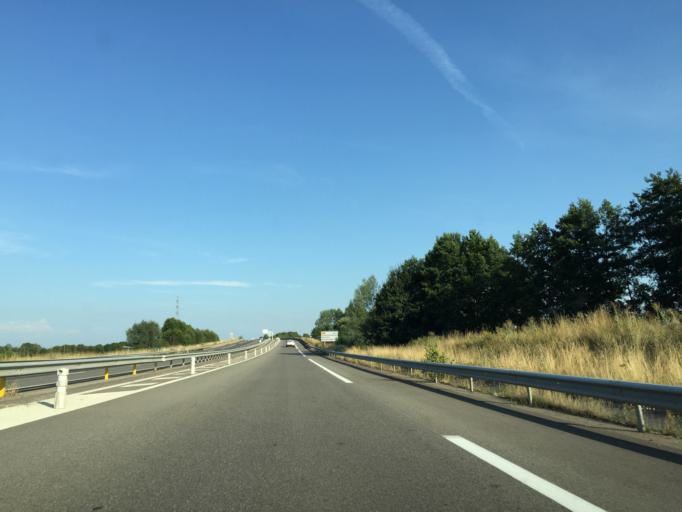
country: FR
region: Alsace
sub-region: Departement du Bas-Rhin
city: Haguenau
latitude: 48.8366
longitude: 7.7807
